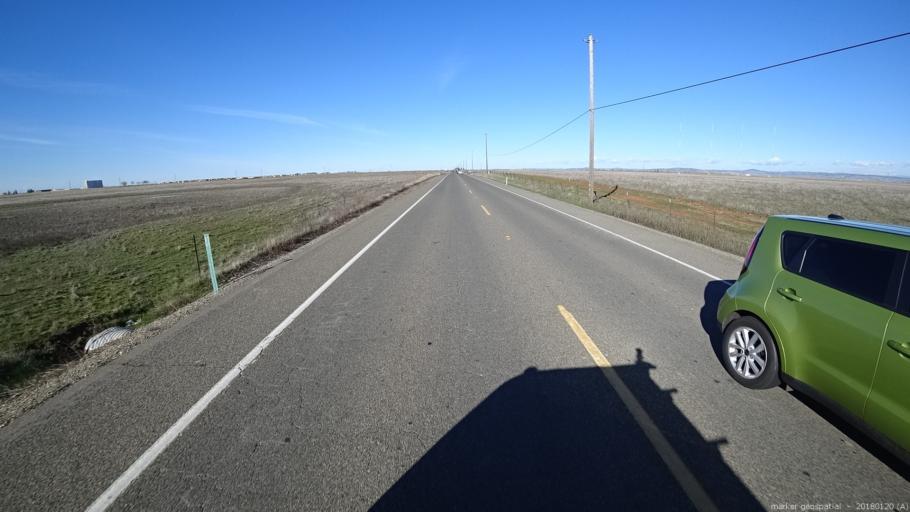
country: US
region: California
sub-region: Sacramento County
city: Gold River
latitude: 38.5510
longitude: -121.1873
